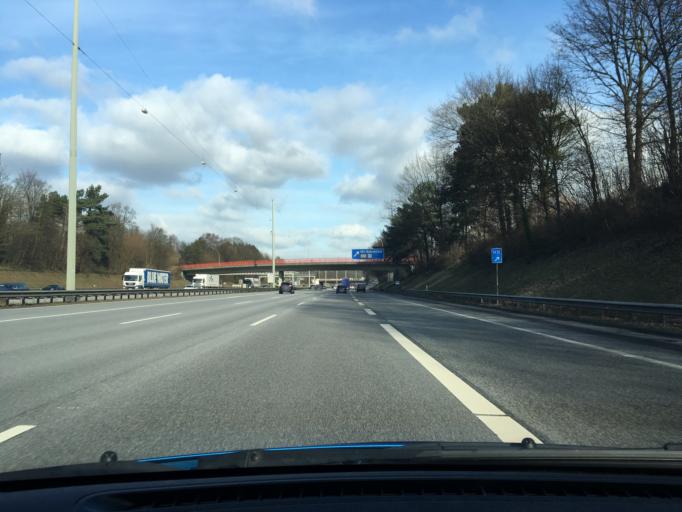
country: DE
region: Hamburg
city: Altona
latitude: 53.5599
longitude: 9.8984
